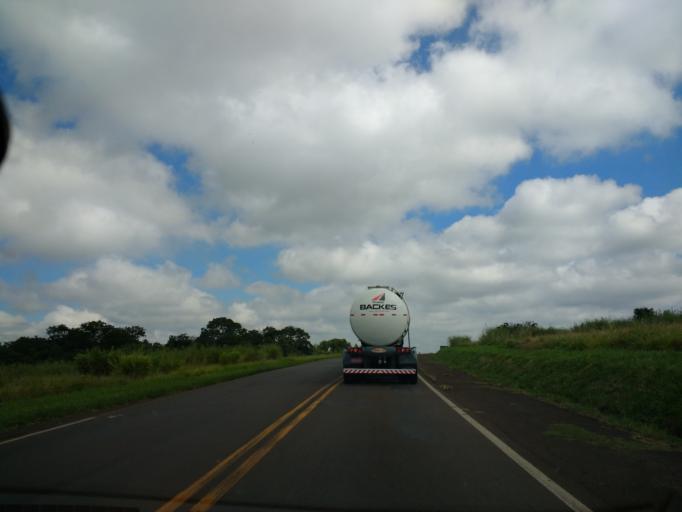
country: BR
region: Parana
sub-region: Cruzeiro Do Oeste
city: Cruzeiro do Oeste
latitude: -23.7718
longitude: -53.0152
